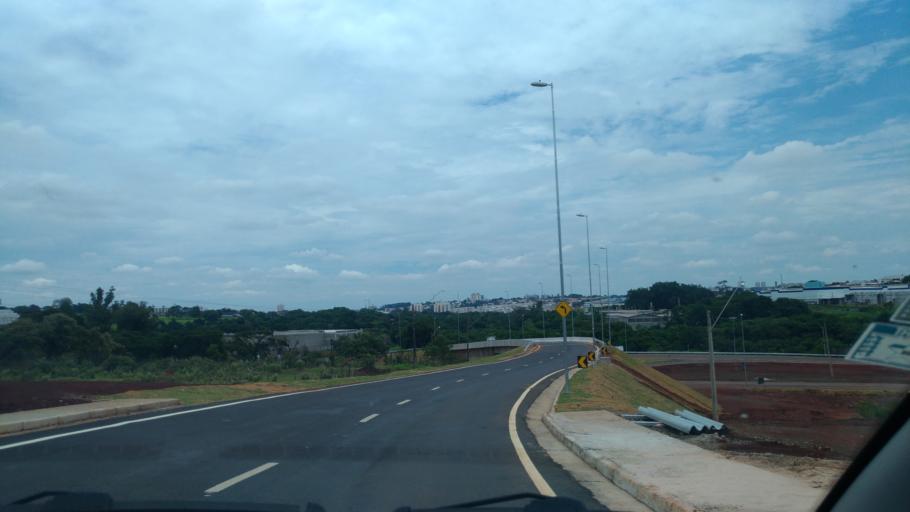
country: BR
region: Sao Paulo
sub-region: Nova Odessa
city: Nova Odessa
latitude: -22.7683
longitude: -47.3156
